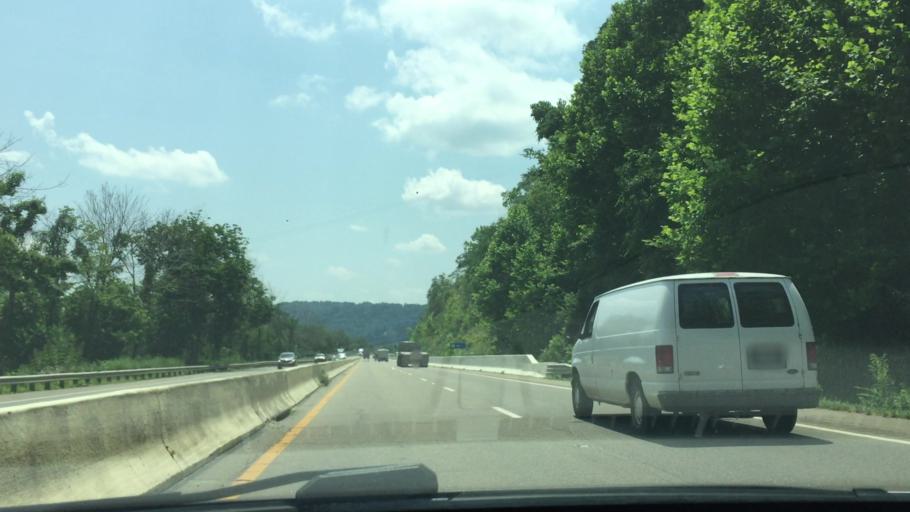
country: US
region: West Virginia
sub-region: Marshall County
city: Moundsville
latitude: 39.9260
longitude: -80.7602
